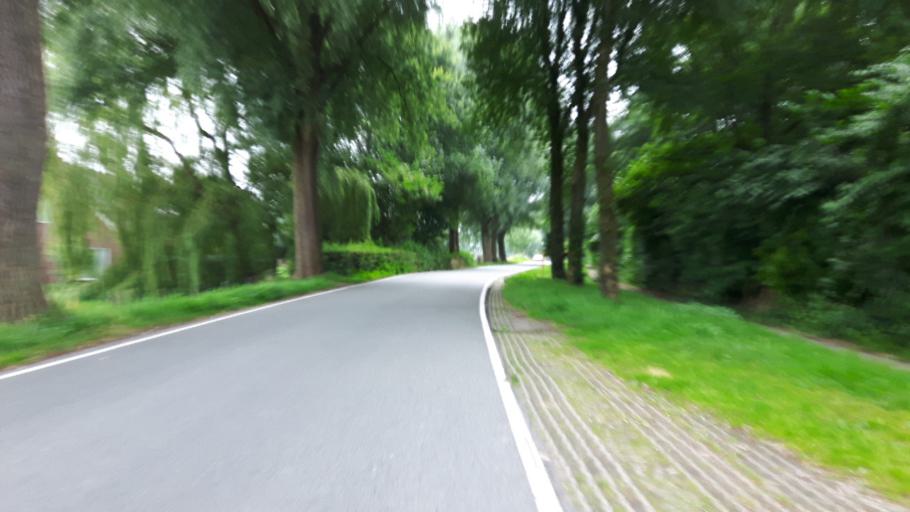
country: NL
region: Utrecht
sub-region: Gemeente IJsselstein
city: IJsselstein
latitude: 52.0353
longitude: 5.0387
